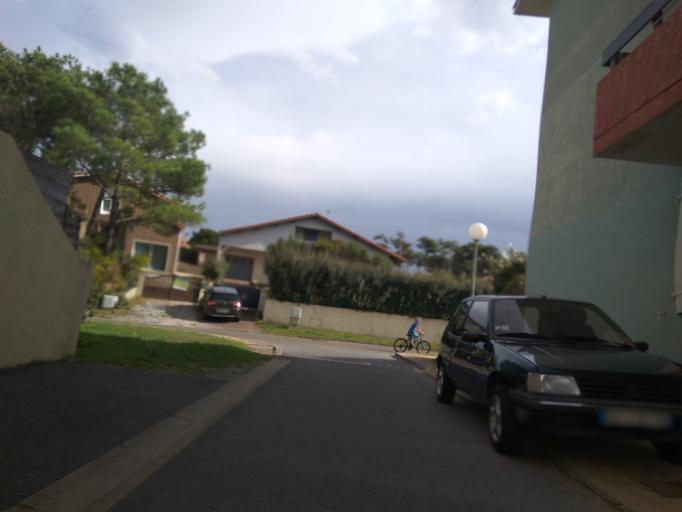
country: FR
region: Aquitaine
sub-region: Departement des Landes
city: Capbreton
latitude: 43.6341
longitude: -1.4458
